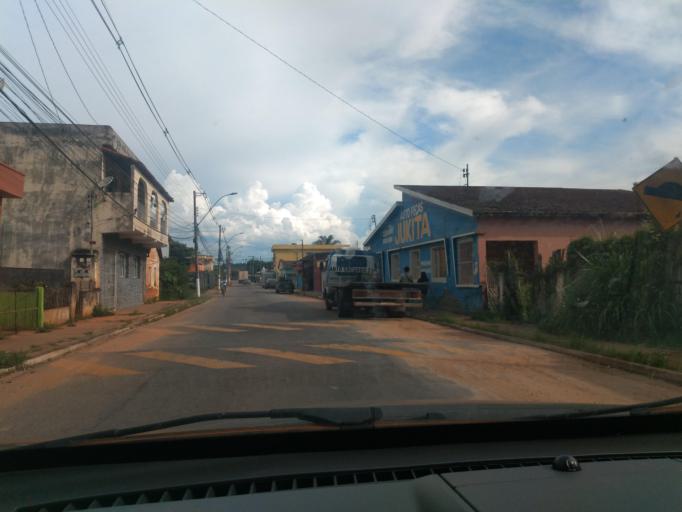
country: BR
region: Minas Gerais
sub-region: Tres Coracoes
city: Tres Coracoes
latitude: -21.7065
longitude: -45.2656
